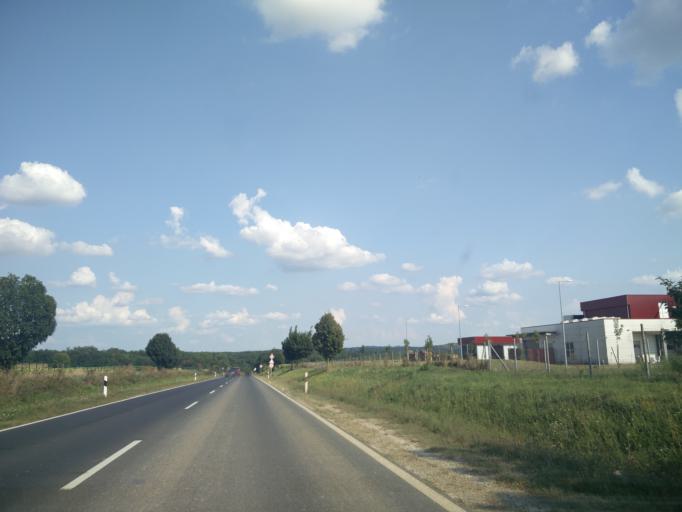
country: HU
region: Zala
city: Zalaegerszeg
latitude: 46.8804
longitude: 16.8386
